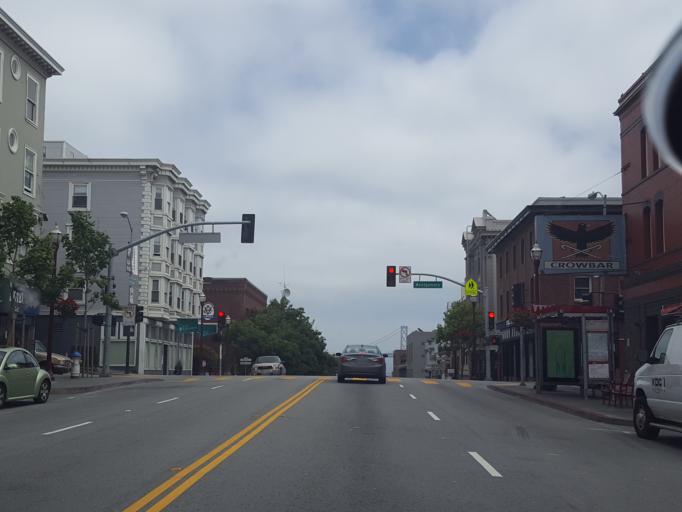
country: US
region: California
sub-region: San Francisco County
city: San Francisco
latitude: 37.7981
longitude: -122.4044
